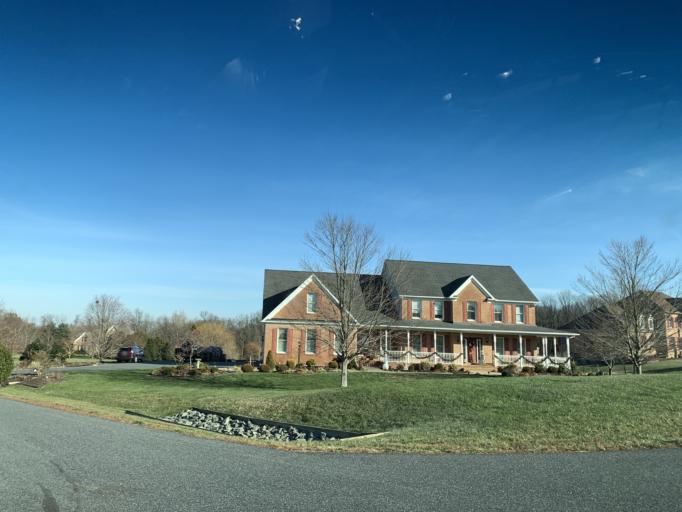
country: US
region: Maryland
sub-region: Harford County
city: South Bel Air
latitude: 39.5688
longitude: -76.2525
